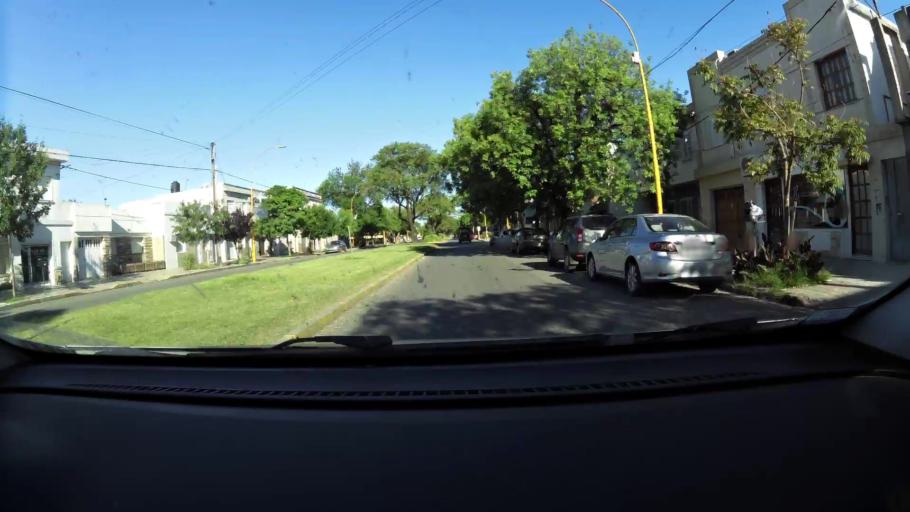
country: AR
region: Cordoba
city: San Francisco
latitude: -31.4317
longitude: -62.0805
